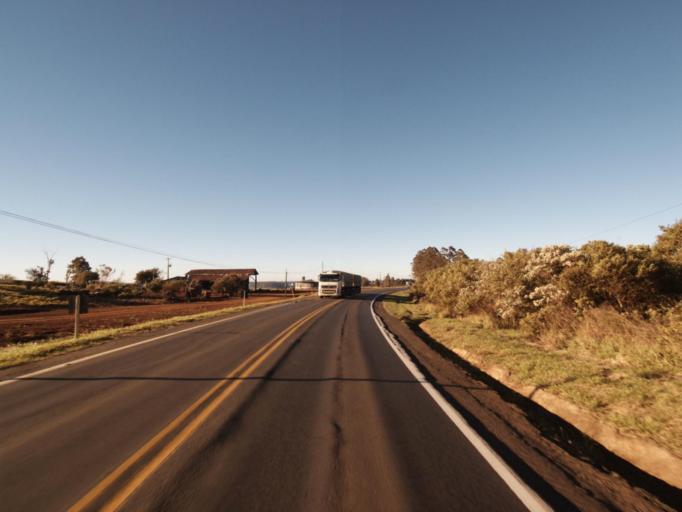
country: AR
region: Misiones
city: Bernardo de Irigoyen
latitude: -26.3076
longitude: -53.5472
